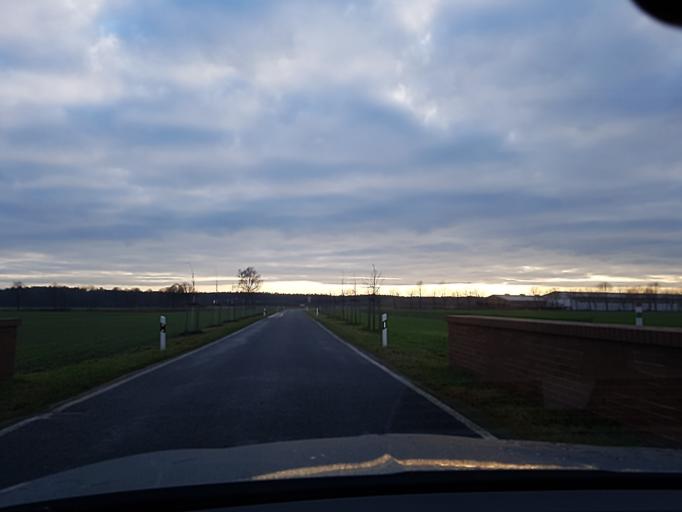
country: DE
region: Brandenburg
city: Schilda
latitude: 51.5790
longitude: 13.3729
